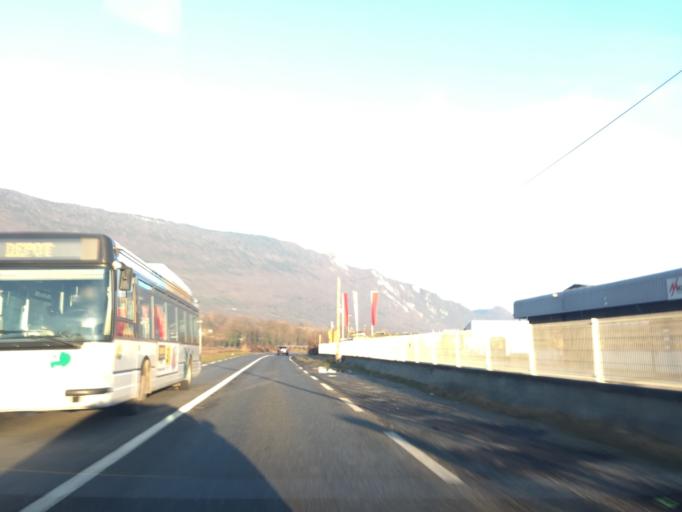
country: FR
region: Rhone-Alpes
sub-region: Departement de la Savoie
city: Voglans
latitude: 45.6220
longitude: 5.8776
